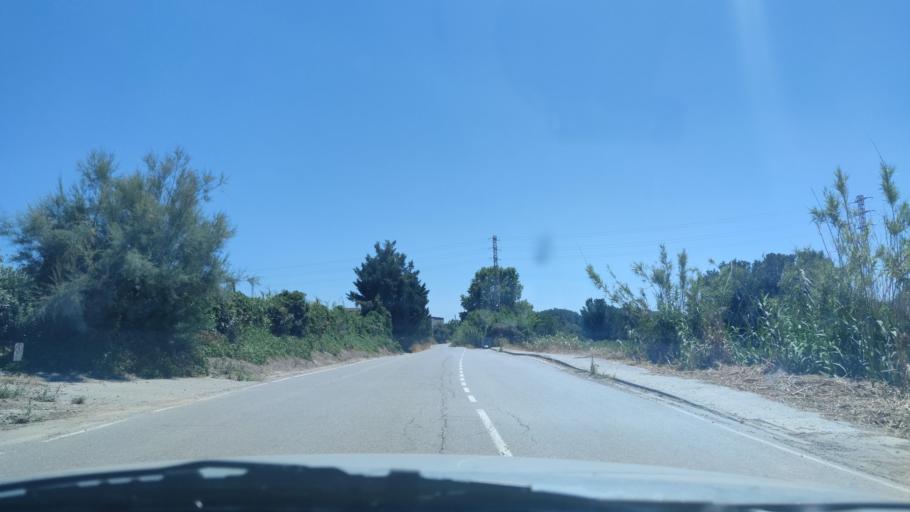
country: ES
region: Catalonia
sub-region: Provincia de Lleida
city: Lleida
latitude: 41.6329
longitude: 0.6562
